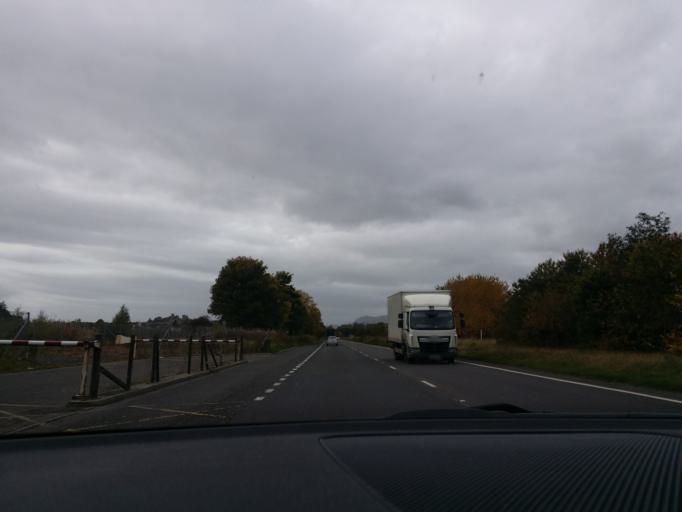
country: GB
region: Scotland
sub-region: Clackmannanshire
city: Clackmannan
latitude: 56.1029
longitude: -3.7275
